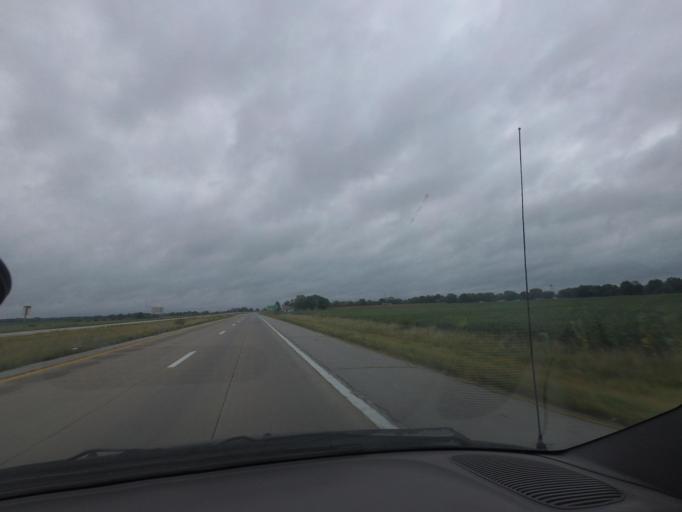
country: US
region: Missouri
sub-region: Marion County
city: Monroe City
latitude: 39.6734
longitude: -91.8688
